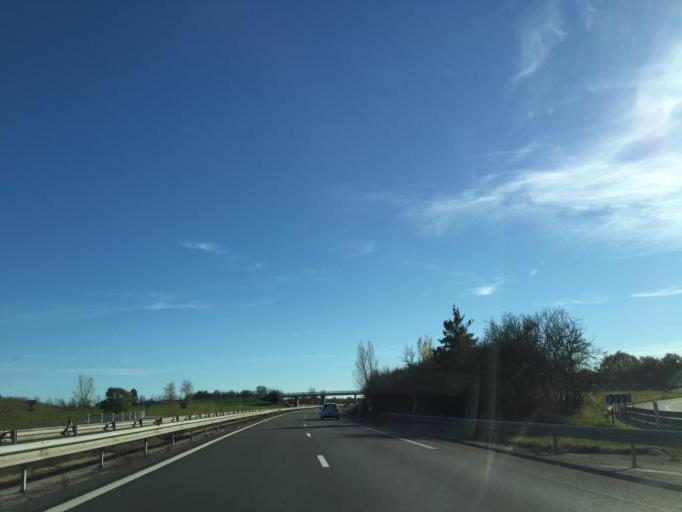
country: FR
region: Rhone-Alpes
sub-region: Departement de la Loire
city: Feurs
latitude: 45.7377
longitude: 4.1818
